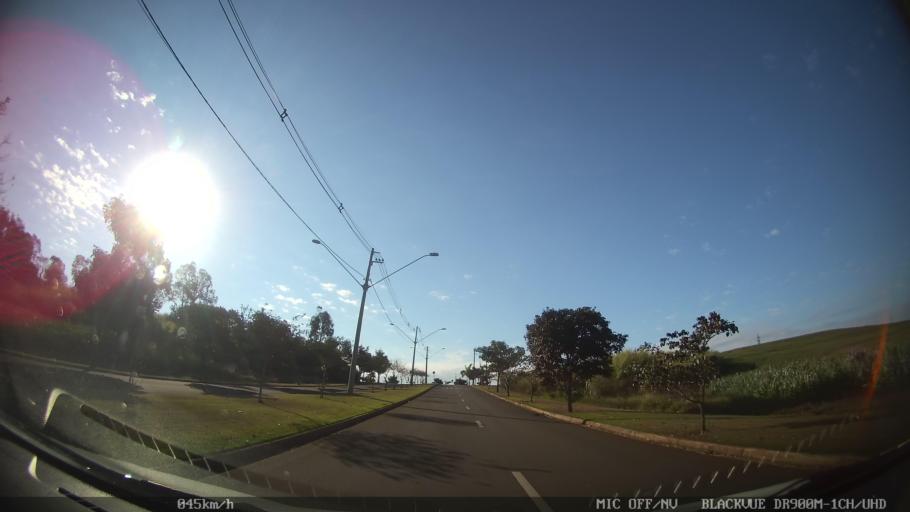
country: BR
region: Sao Paulo
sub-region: Piracicaba
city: Piracicaba
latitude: -22.6931
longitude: -47.6154
